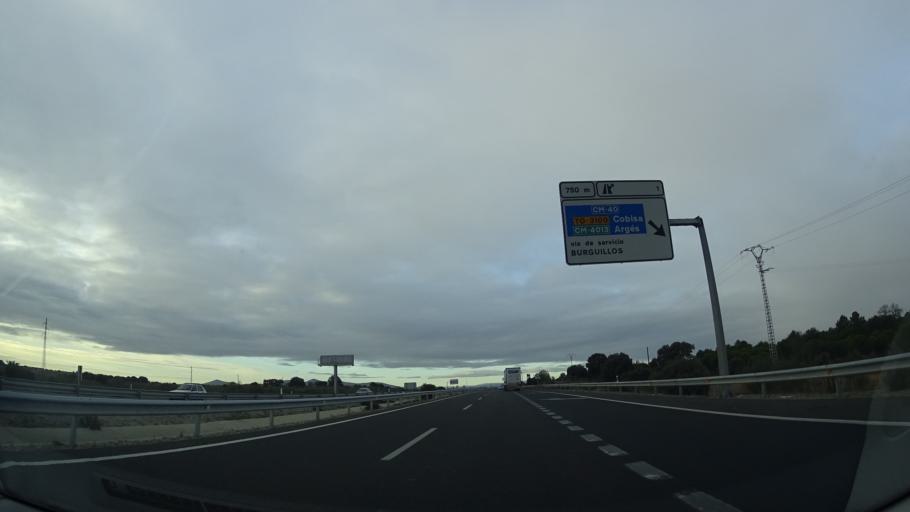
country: ES
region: Castille-La Mancha
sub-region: Province of Toledo
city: Burguillos de Toledo
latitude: 39.8324
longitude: -3.9800
